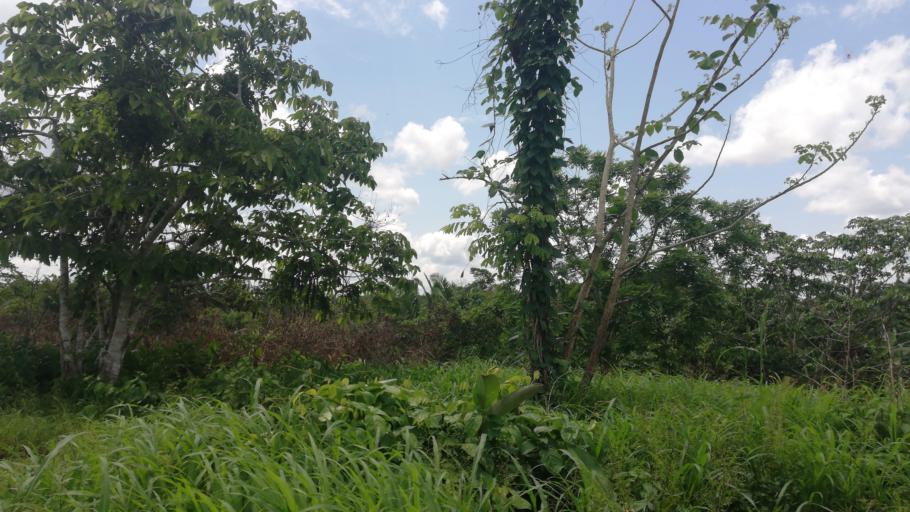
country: PE
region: Ucayali
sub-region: Provincia de Coronel Portillo
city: Puerto Callao
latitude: -8.2708
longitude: -74.6543
